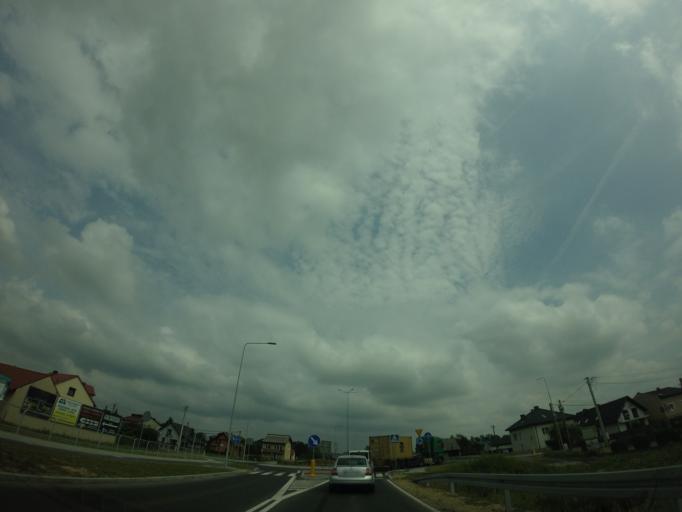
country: PL
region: Lesser Poland Voivodeship
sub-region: Powiat oswiecimski
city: Zaborze
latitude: 50.0549
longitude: 19.2615
